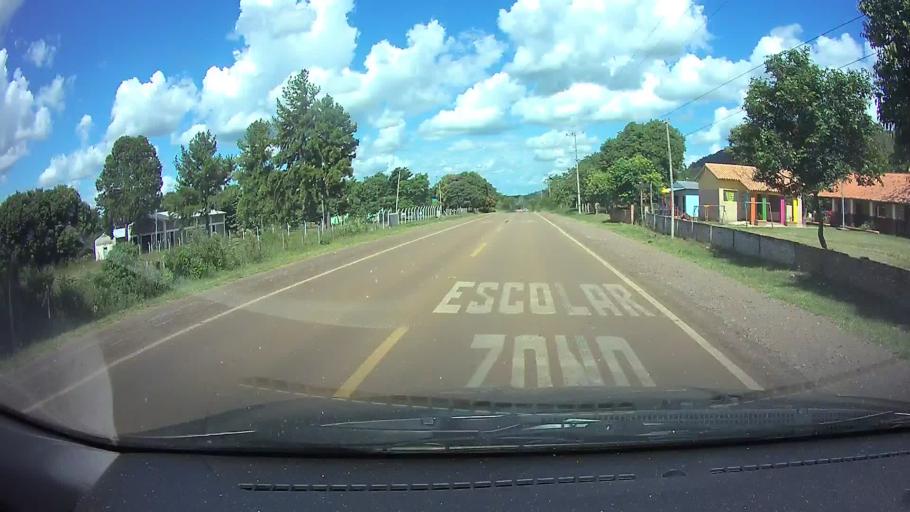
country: PY
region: Paraguari
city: La Colmena
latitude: -25.9148
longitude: -56.7447
